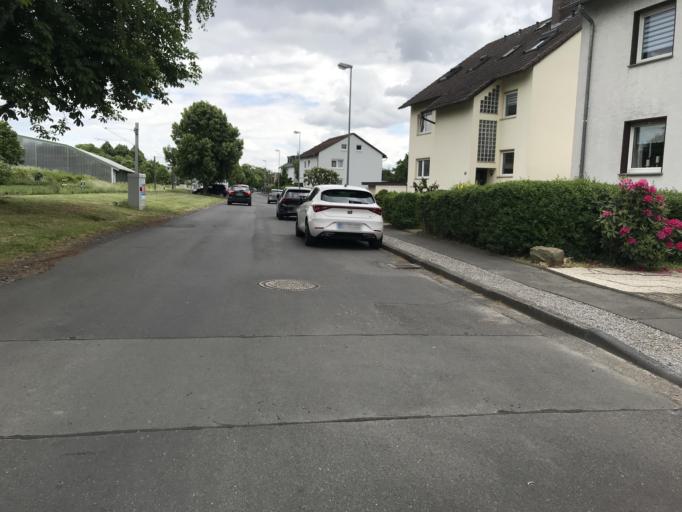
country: DE
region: Hesse
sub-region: Regierungsbezirk Kassel
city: Baunatal
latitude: 51.2530
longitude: 9.3864
